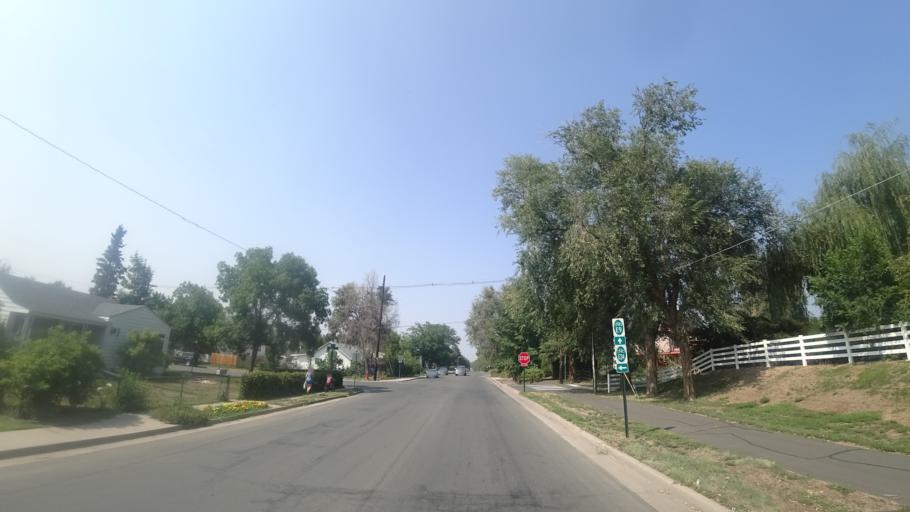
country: US
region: Colorado
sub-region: Arapahoe County
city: Englewood
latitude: 39.6418
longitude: -104.9784
